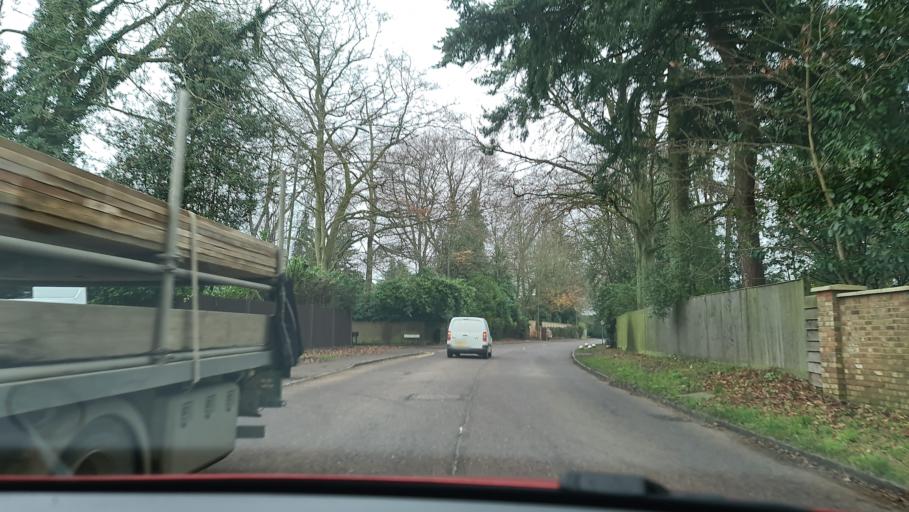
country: GB
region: England
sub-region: Buckinghamshire
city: Beaconsfield
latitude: 51.6170
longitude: -0.6486
